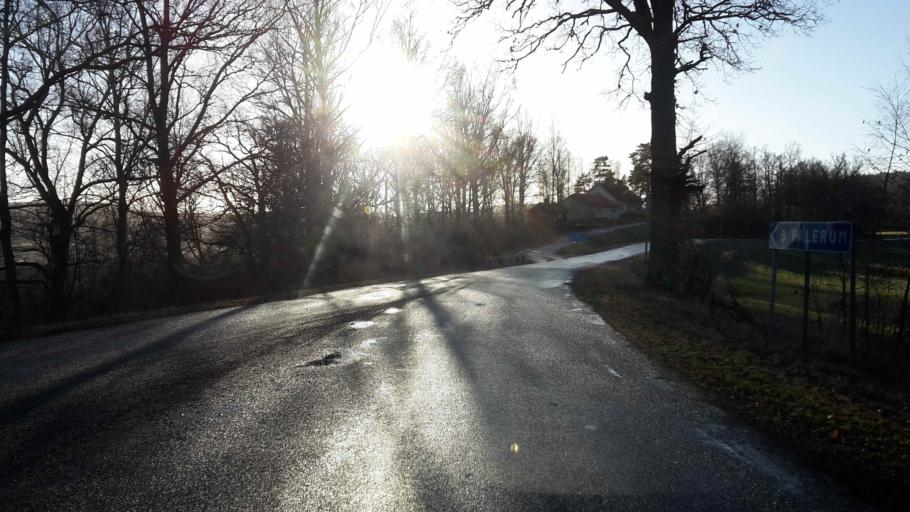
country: SE
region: Kalmar
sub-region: Vasterviks Kommun
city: Overum
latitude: 58.1512
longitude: 16.3246
